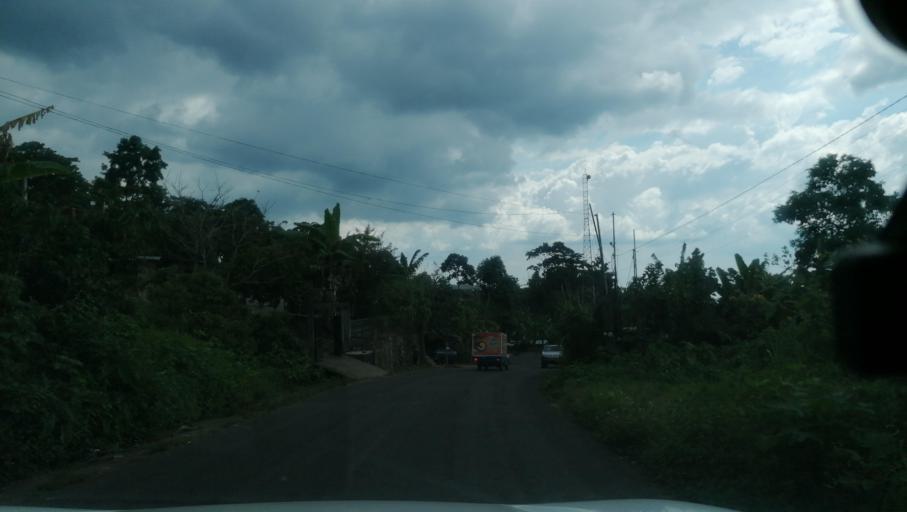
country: MX
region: Chiapas
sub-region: Cacahoatan
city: Benito Juarez
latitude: 15.0810
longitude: -92.1971
